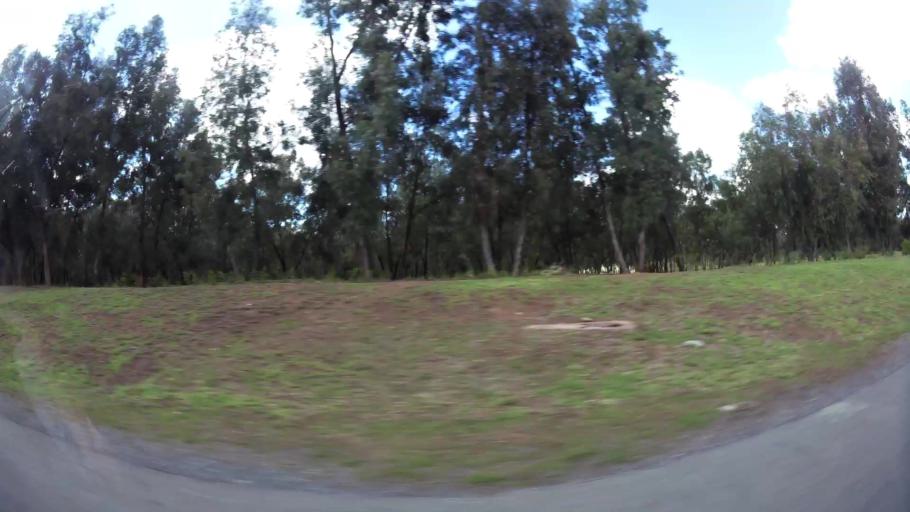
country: MA
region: Chaouia-Ouardigha
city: Nouaseur
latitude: 33.3769
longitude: -7.5735
